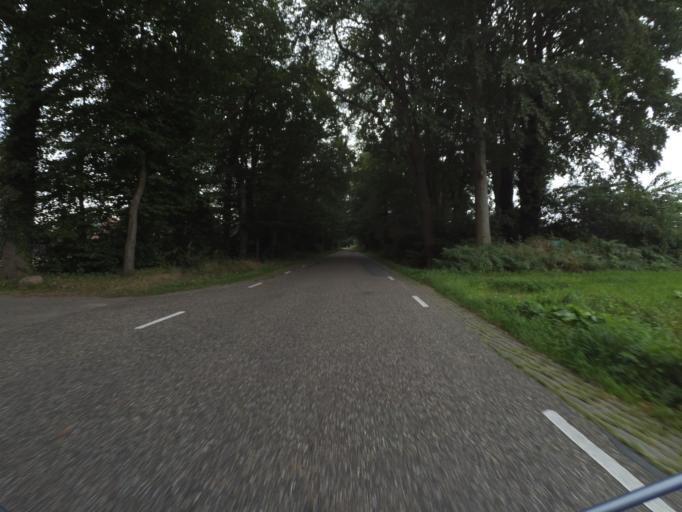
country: NL
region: Overijssel
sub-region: Gemeente Losser
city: Losser
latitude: 52.2861
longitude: 7.0191
